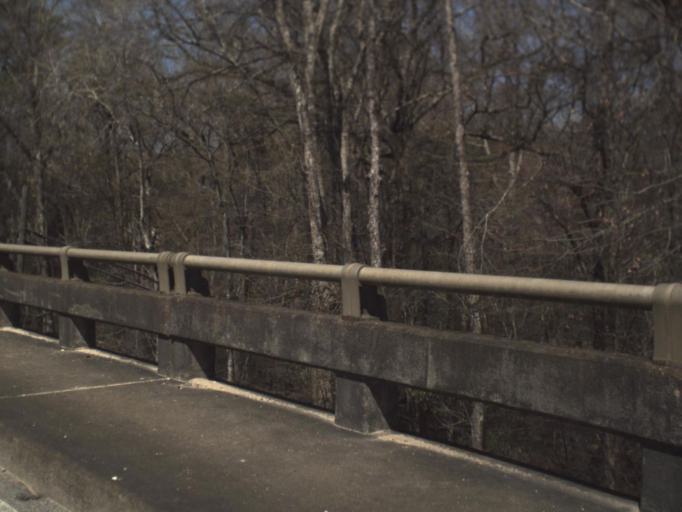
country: US
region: Florida
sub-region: Jackson County
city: Marianna
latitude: 30.7730
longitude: -85.2157
